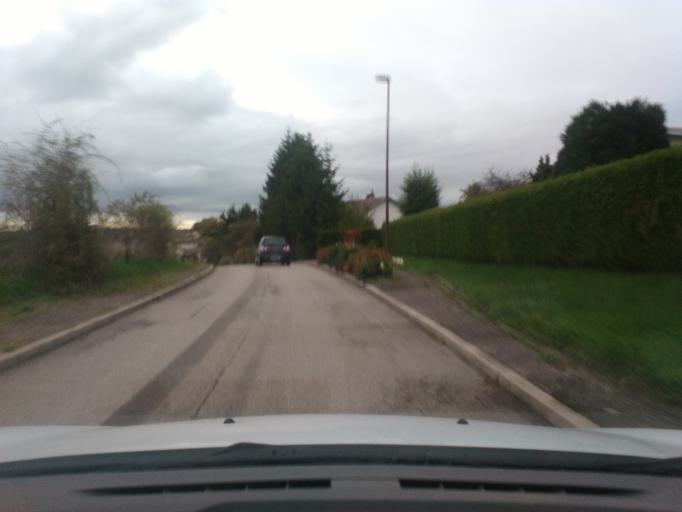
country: FR
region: Lorraine
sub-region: Departement des Vosges
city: Deyvillers
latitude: 48.1969
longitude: 6.4902
